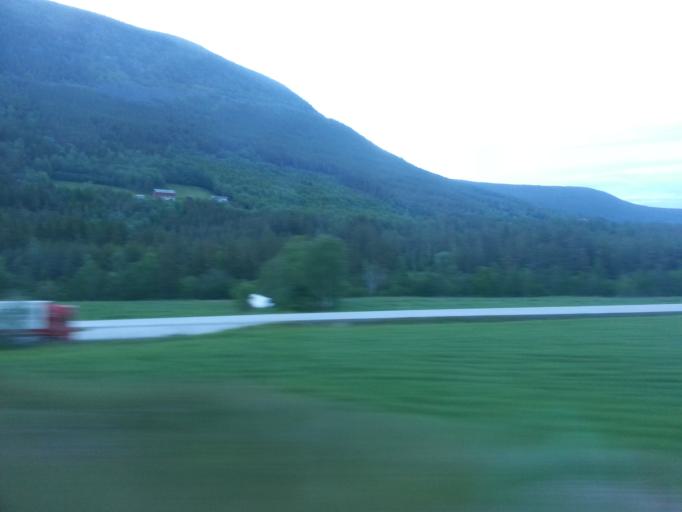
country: NO
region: Oppland
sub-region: Dovre
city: Dovre
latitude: 61.9393
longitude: 9.3028
